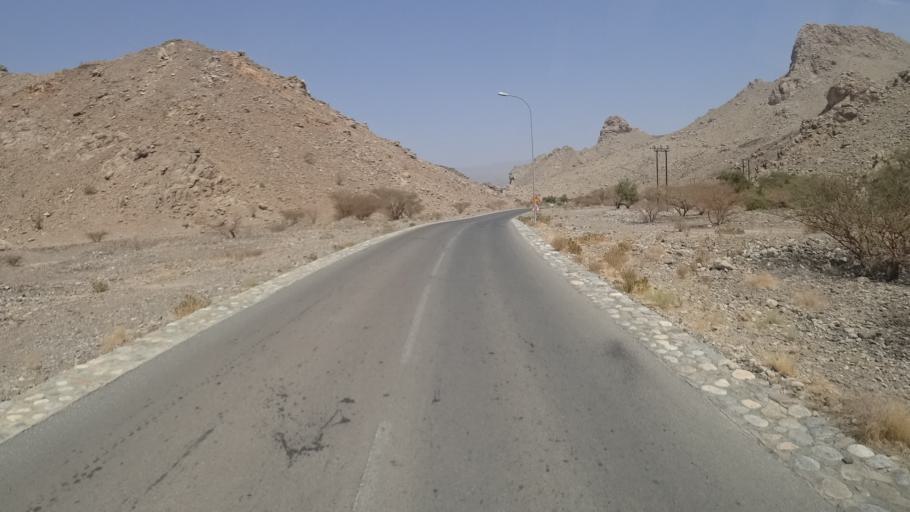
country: OM
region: Muhafazat ad Dakhiliyah
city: Bahla'
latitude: 23.0490
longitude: 57.3131
